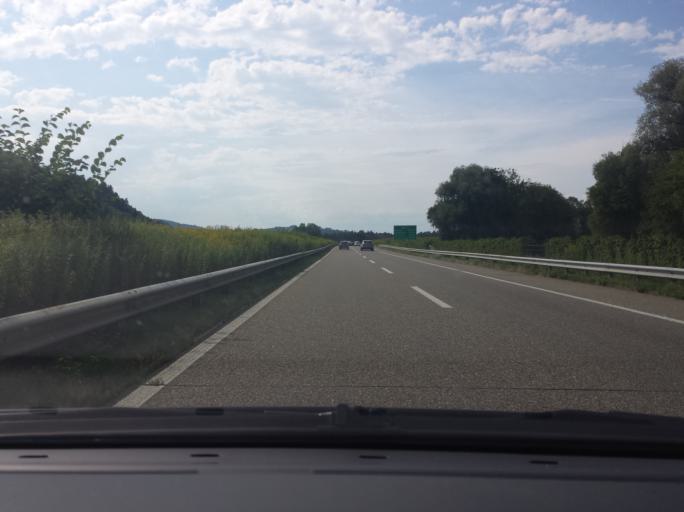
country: CH
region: Saint Gallen
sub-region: Wahlkreis Rheintal
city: Sankt Margrethen
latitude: 47.4575
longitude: 9.6214
